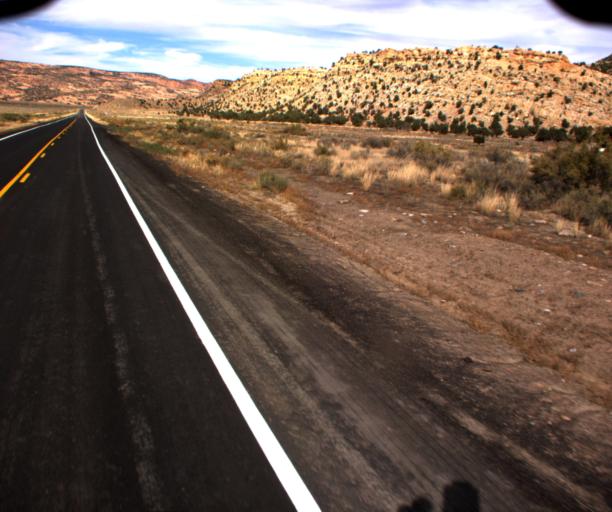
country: US
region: Arizona
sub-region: Navajo County
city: Kayenta
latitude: 36.5949
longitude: -110.4723
